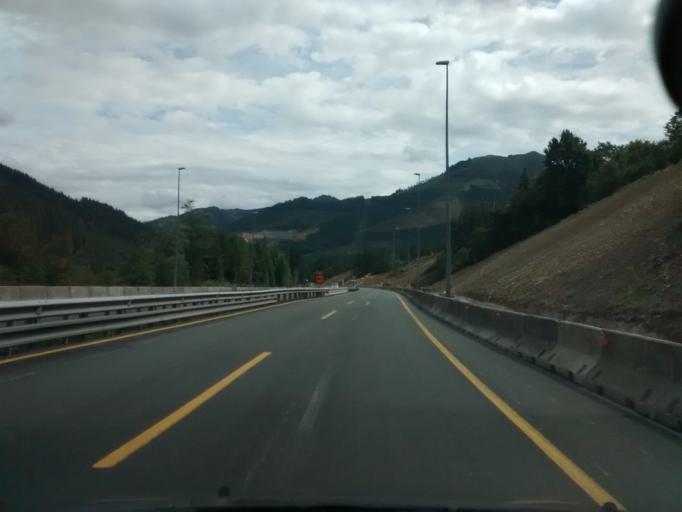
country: ES
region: Basque Country
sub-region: Bizkaia
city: Zaldibar
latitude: 43.1768
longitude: -2.5246
